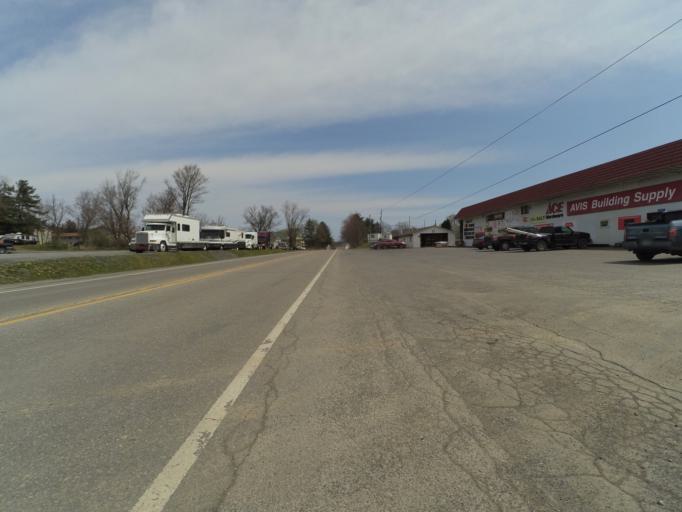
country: US
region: Pennsylvania
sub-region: Clinton County
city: Avis
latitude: 41.1828
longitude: -77.3236
